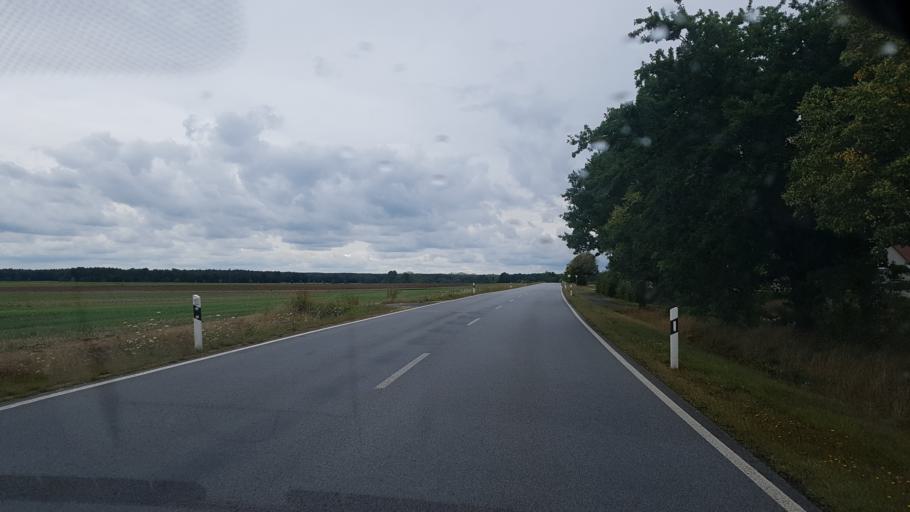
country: DE
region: Saxony
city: Niesky
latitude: 51.2527
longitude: 14.8067
